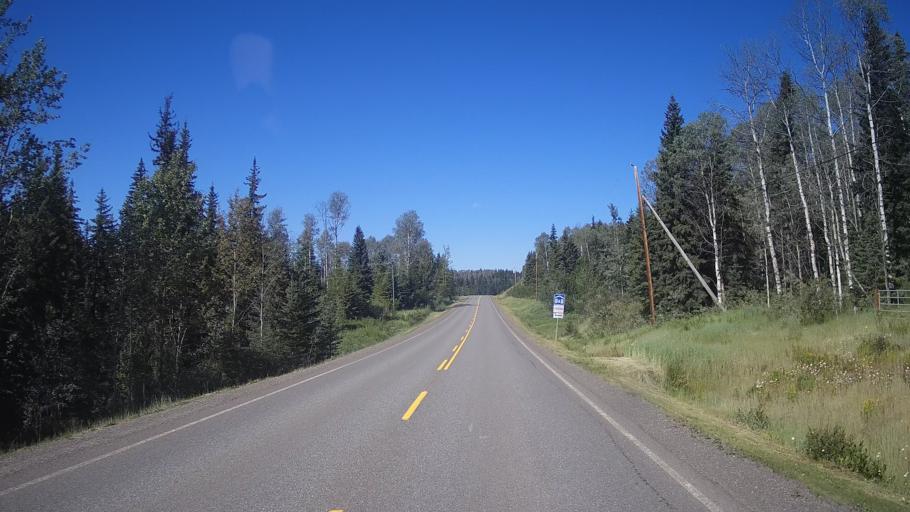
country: CA
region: British Columbia
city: Kamloops
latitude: 51.5040
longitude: -120.6169
